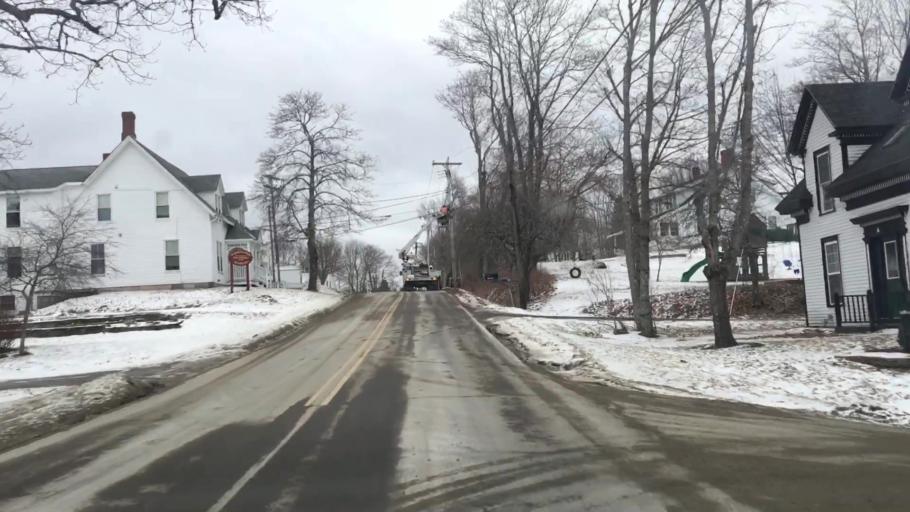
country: US
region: Maine
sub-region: Washington County
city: East Machias
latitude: 44.7354
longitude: -67.3888
